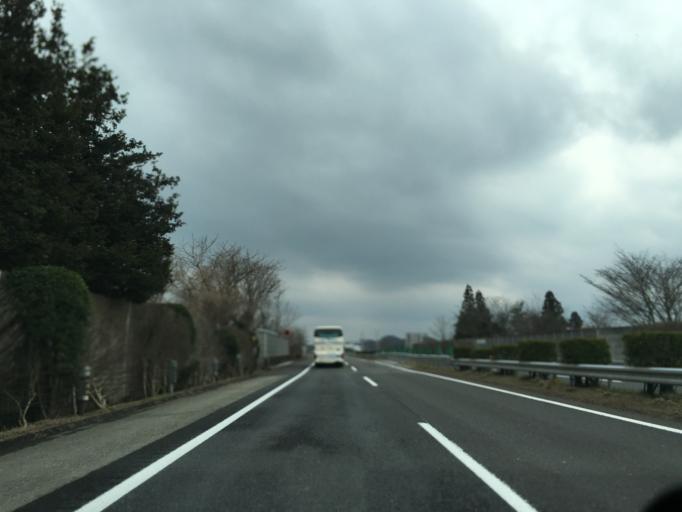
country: JP
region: Tochigi
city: Kuroiso
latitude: 37.1293
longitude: 140.1796
